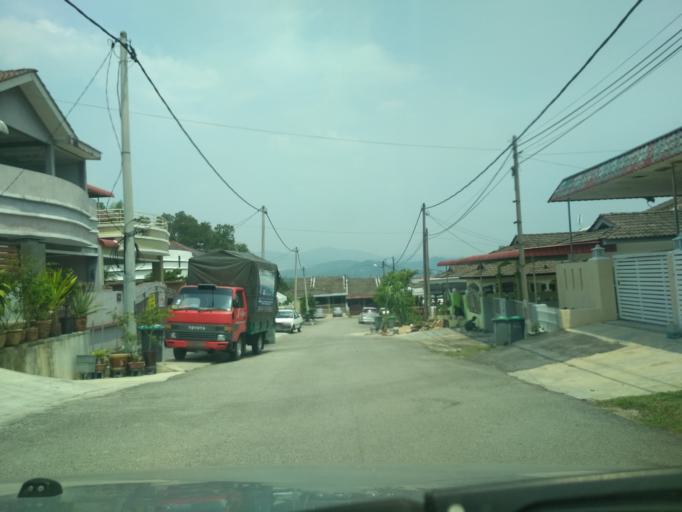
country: MY
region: Kedah
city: Kulim
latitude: 5.3579
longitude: 100.5325
